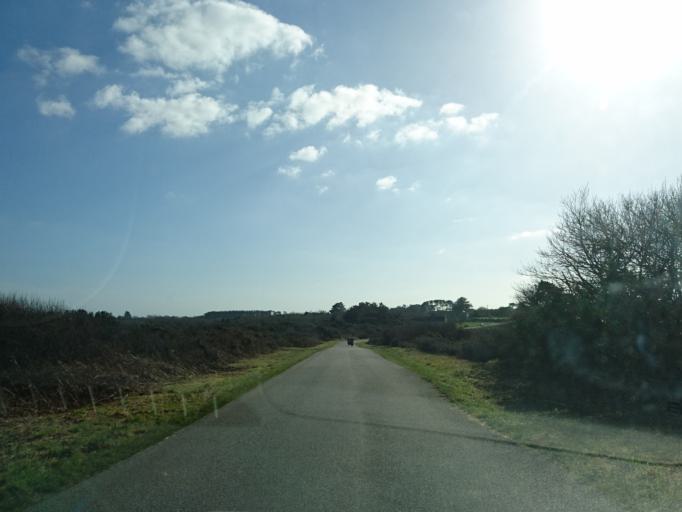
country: FR
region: Brittany
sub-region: Departement du Finistere
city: Roscanvel
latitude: 48.3283
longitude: -4.5688
